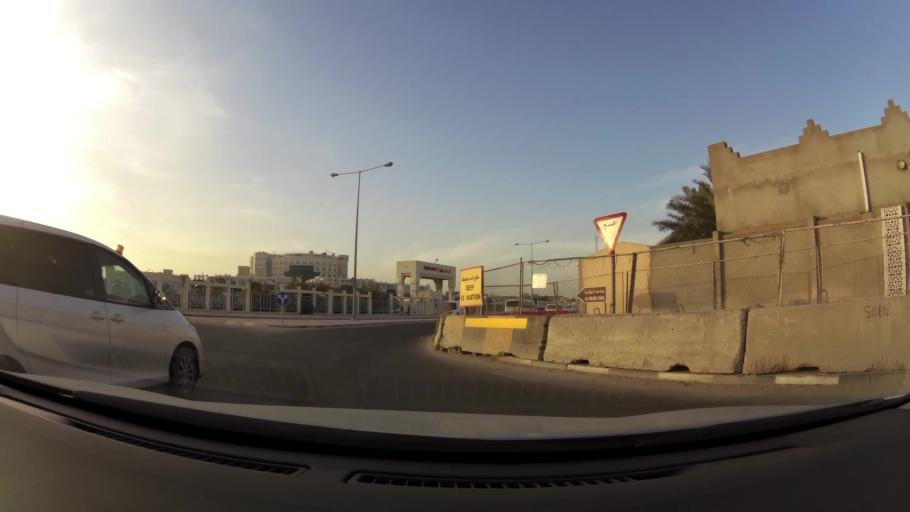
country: QA
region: Al Wakrah
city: Al Wakrah
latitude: 25.1646
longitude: 51.5903
